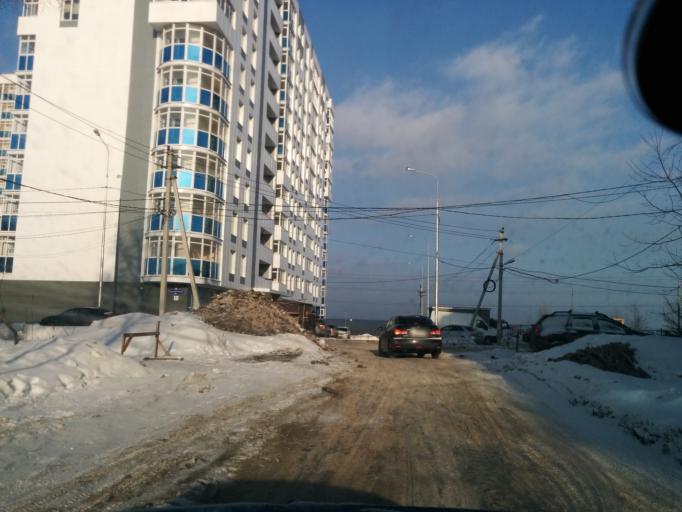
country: RU
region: Perm
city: Perm
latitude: 58.0212
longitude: 56.2664
